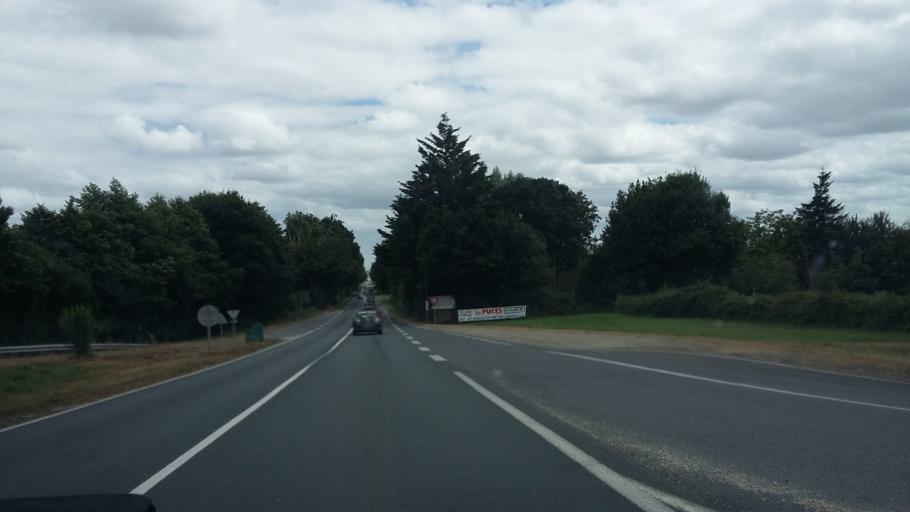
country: FR
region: Pays de la Loire
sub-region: Departement de la Vendee
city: Saint-Christophe-du-Ligneron
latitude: 46.8202
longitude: -1.7642
